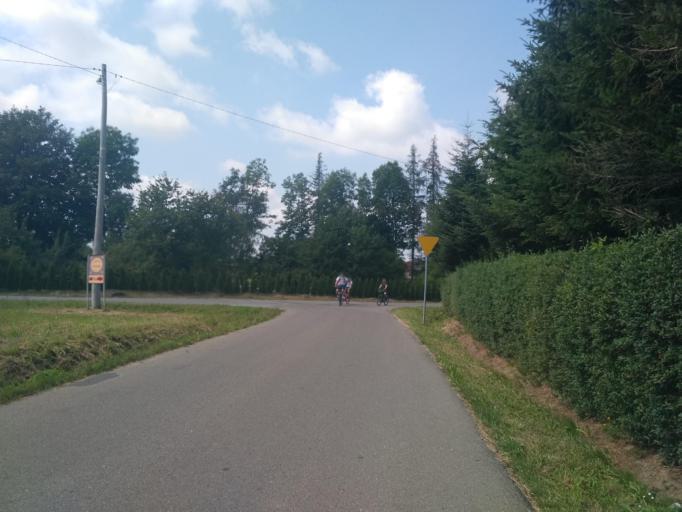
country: PL
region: Subcarpathian Voivodeship
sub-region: Powiat lancucki
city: Kraczkowa
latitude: 50.0355
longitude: 22.1920
